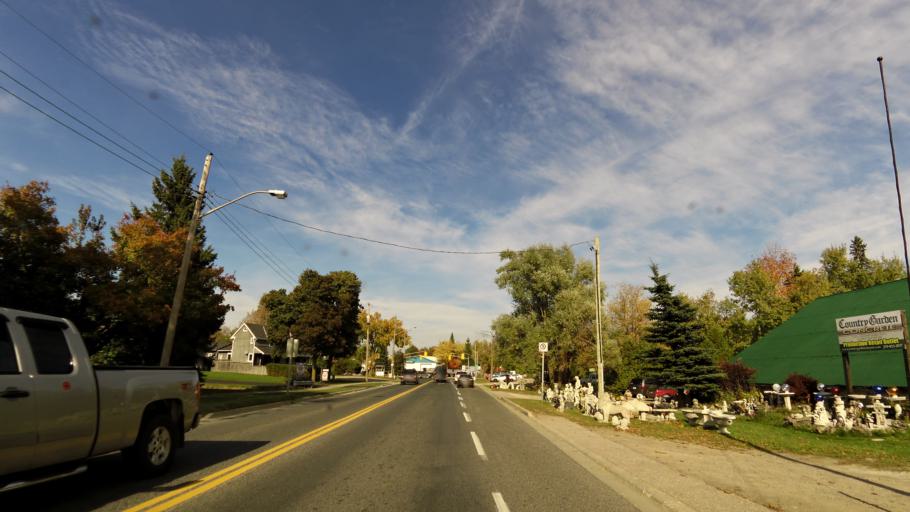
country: CA
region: Ontario
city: Orangeville
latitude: 43.7647
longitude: -80.0587
